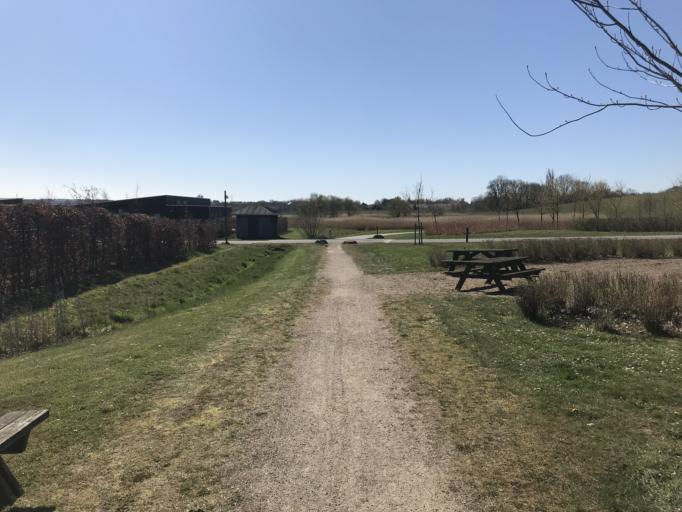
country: DK
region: Capital Region
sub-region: Hoje-Taastrup Kommune
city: Flong
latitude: 55.6594
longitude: 12.1498
